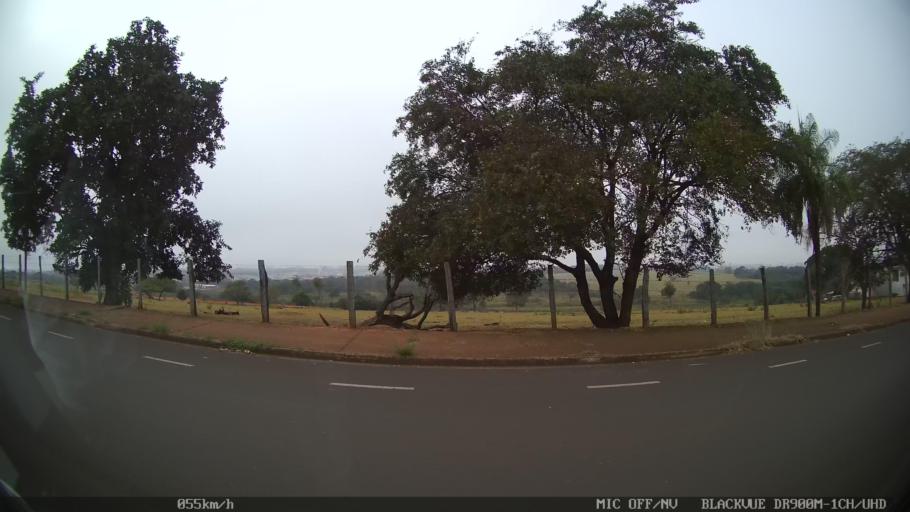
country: BR
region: Sao Paulo
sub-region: Sao Jose Do Rio Preto
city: Sao Jose do Rio Preto
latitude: -20.8549
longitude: -49.3711
